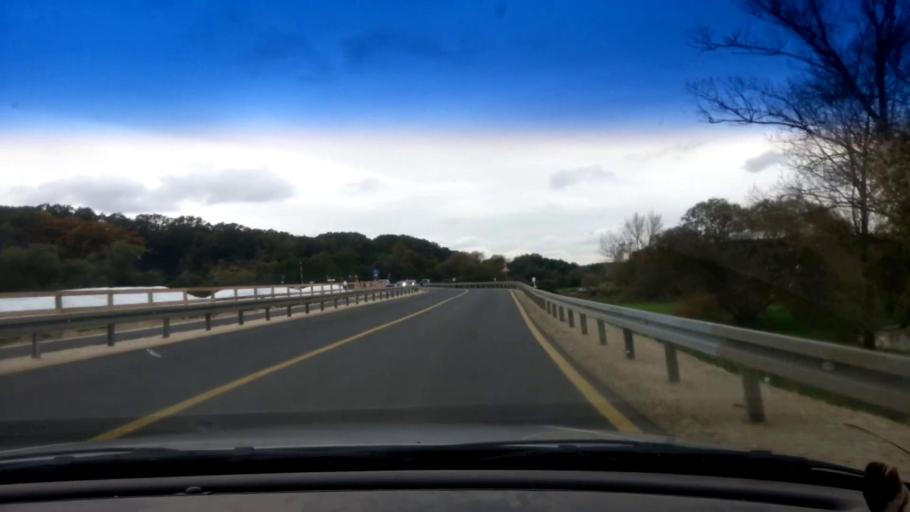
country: DE
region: Bavaria
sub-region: Upper Franconia
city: Baunach
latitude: 49.9778
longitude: 10.8603
